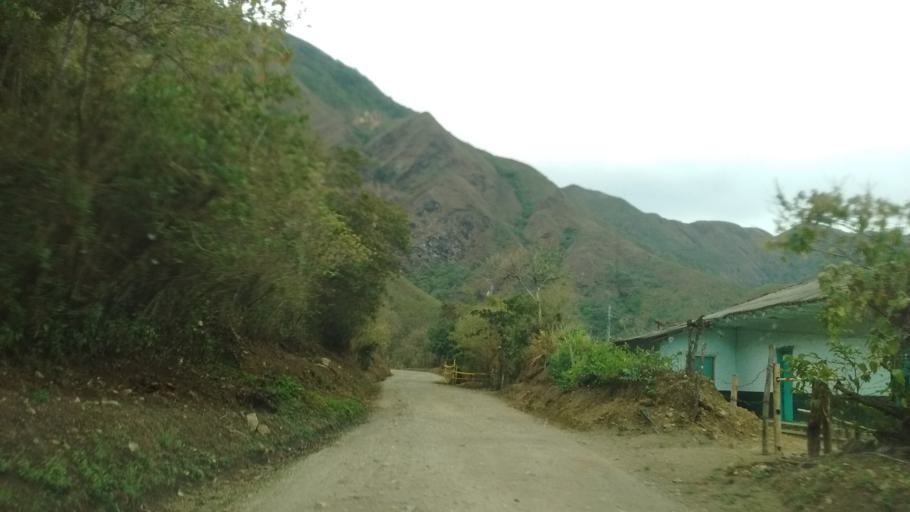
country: CO
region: Cauca
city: Almaguer
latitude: 1.8448
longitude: -76.9061
